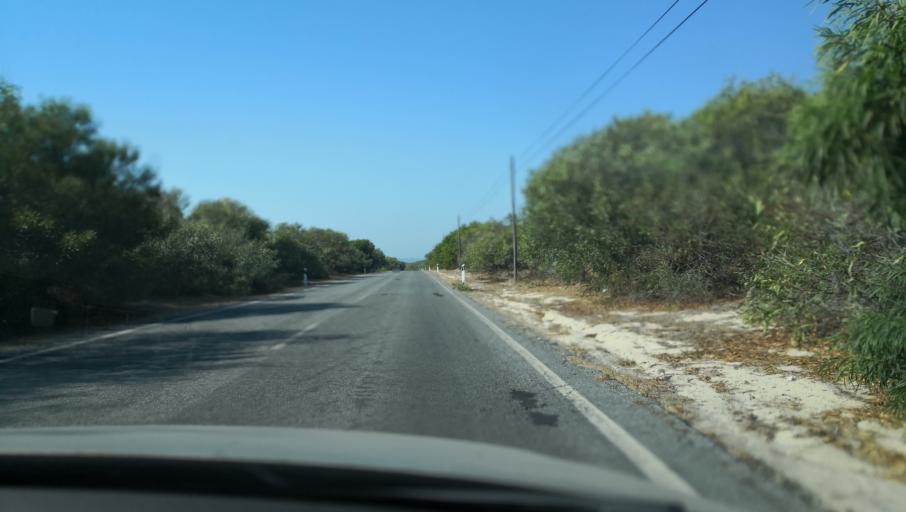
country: PT
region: Setubal
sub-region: Setubal
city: Setubal
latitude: 38.4047
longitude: -8.8087
